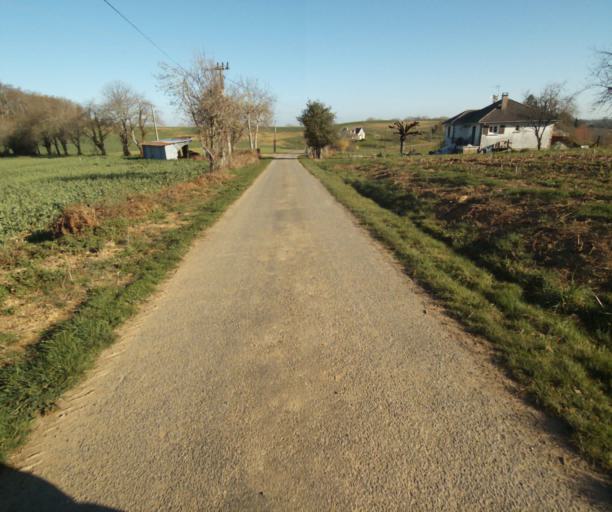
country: FR
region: Limousin
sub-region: Departement de la Correze
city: Uzerche
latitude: 45.3905
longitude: 1.6196
